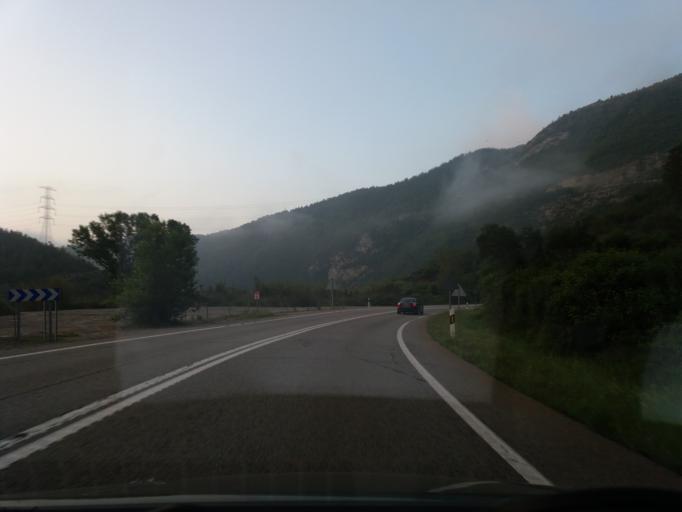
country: ES
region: Catalonia
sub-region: Provincia de Barcelona
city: Collbato
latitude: 41.5727
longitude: 1.8632
